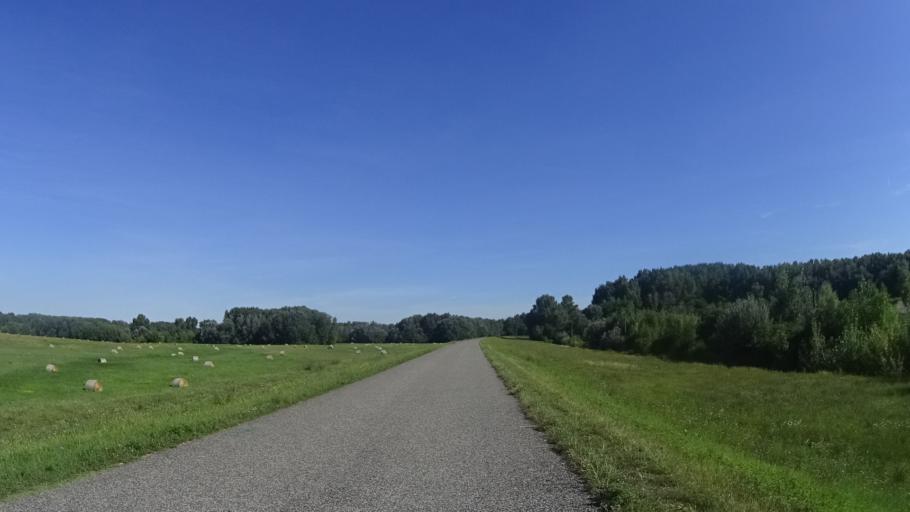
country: SK
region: Bratislavsky
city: Bratislava
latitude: 48.1066
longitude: 17.1466
